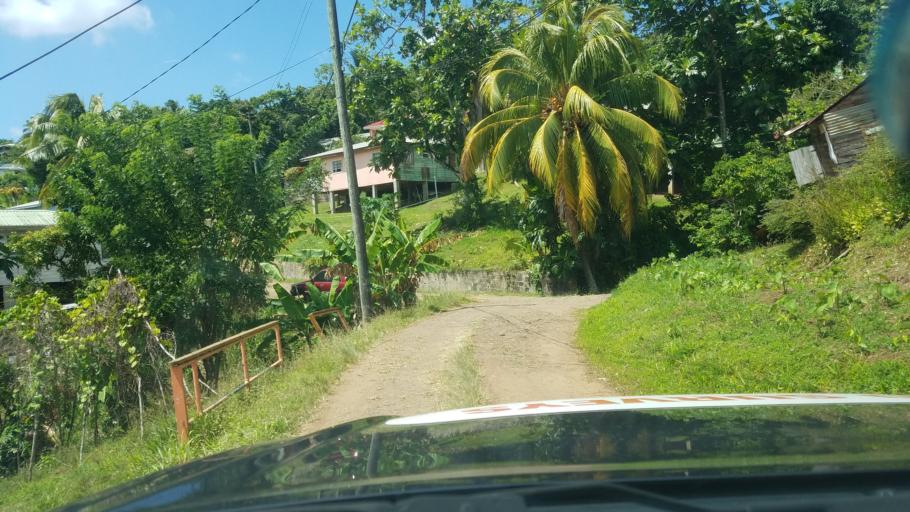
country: LC
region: Castries Quarter
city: Bisee
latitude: 14.0288
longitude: -60.9527
